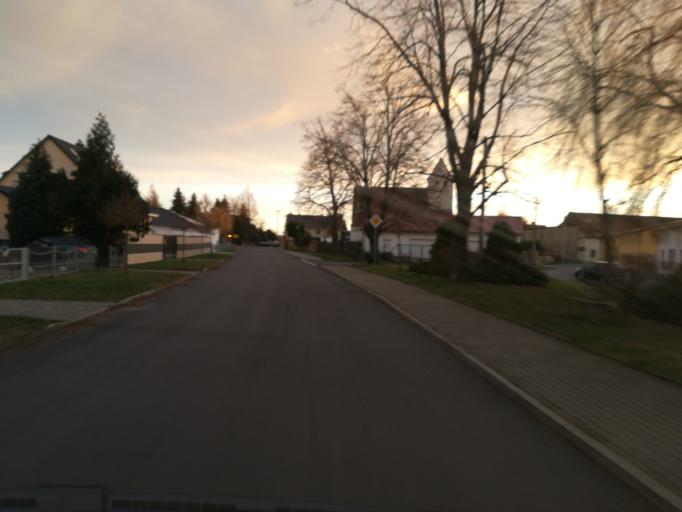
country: DE
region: Saxony
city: Wiedemar
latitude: 51.4976
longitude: 12.2282
